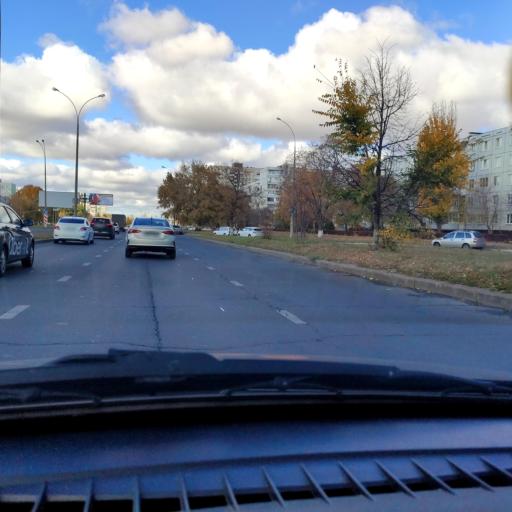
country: RU
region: Samara
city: Tol'yatti
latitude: 53.5284
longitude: 49.2889
